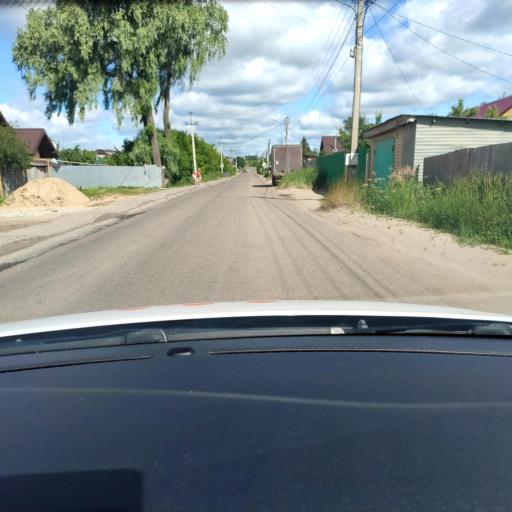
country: RU
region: Tatarstan
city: Vysokaya Gora
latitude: 55.8601
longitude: 49.2404
